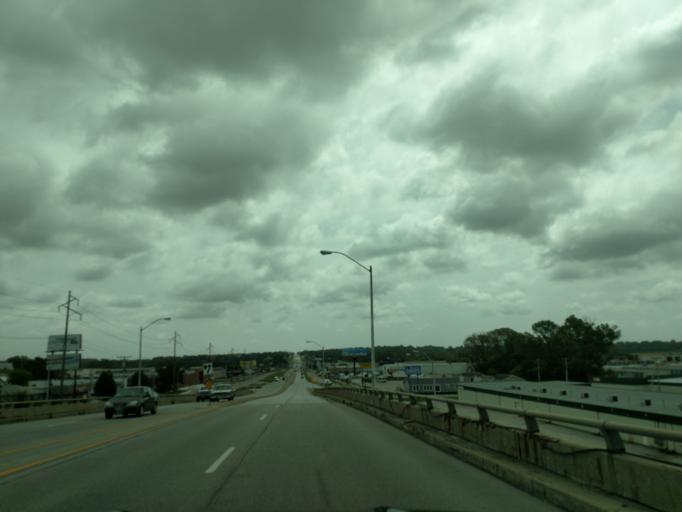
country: US
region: Nebraska
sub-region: Douglas County
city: Ralston
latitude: 41.2124
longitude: -96.0236
